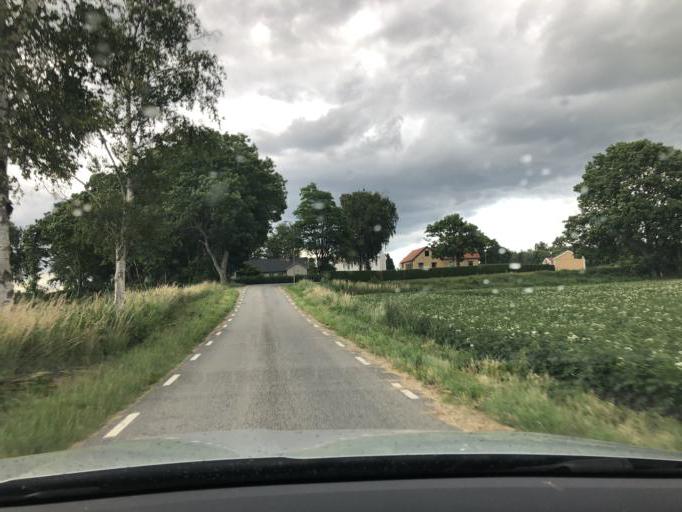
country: SE
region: Blekinge
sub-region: Solvesborgs Kommun
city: Soelvesborg
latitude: 56.1080
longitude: 14.6275
